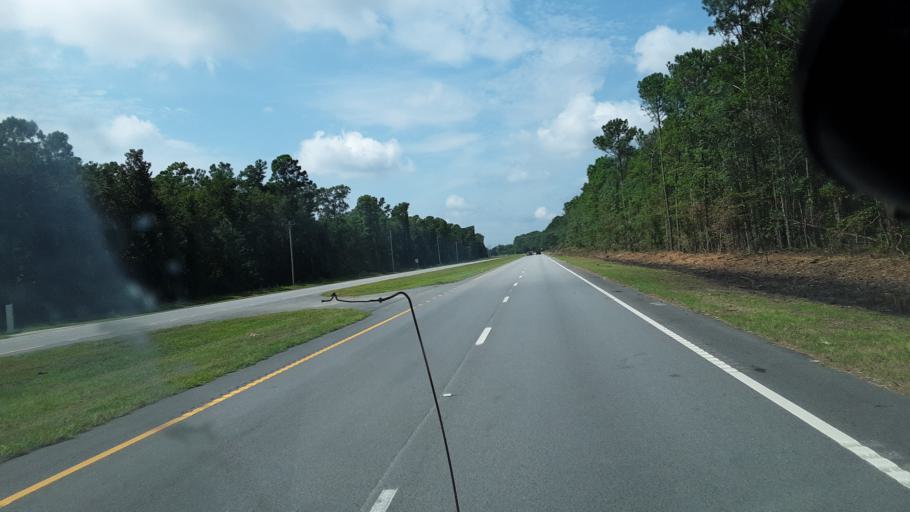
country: US
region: South Carolina
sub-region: Charleston County
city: Awendaw
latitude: 33.0655
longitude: -79.5318
